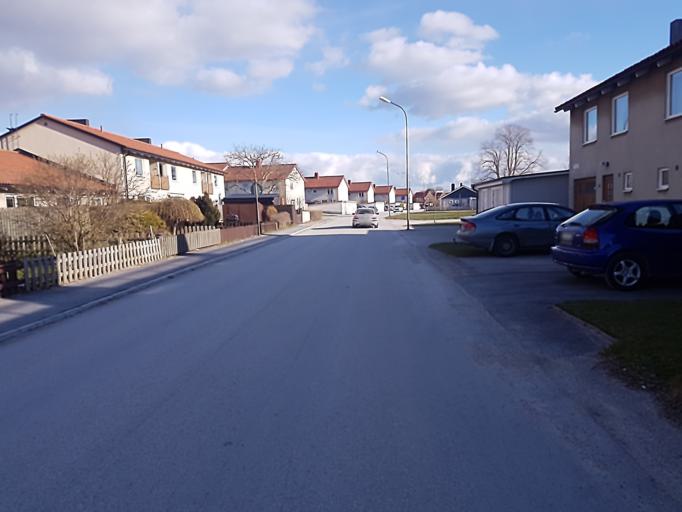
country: SE
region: Gotland
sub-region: Gotland
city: Visby
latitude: 57.6178
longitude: 18.2911
